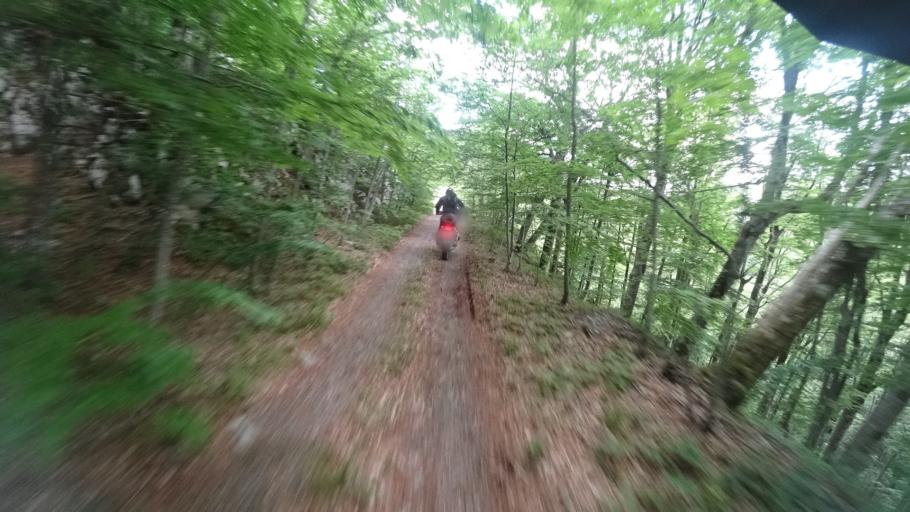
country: HR
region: Licko-Senjska
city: Gospic
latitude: 44.4300
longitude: 15.2862
